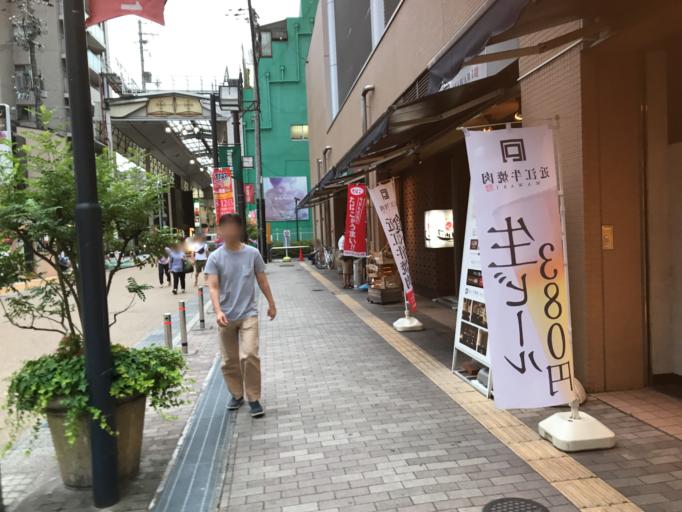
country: JP
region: Shiga Prefecture
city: Kusatsu
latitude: 35.0201
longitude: 135.9623
